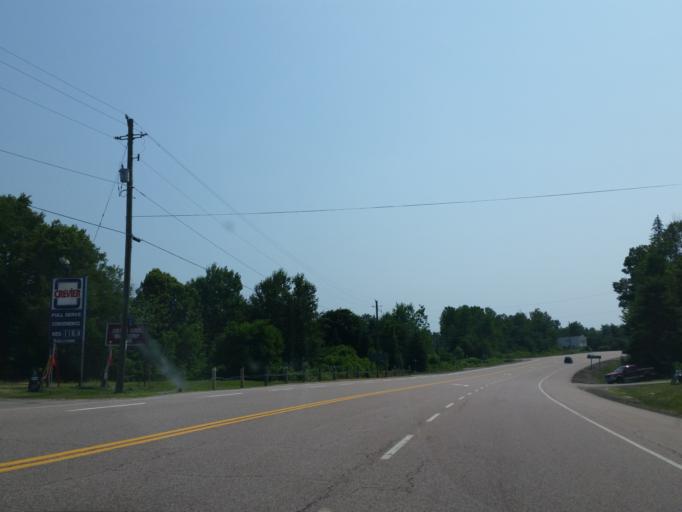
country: CA
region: Ontario
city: Deep River
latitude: 46.2131
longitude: -77.8967
